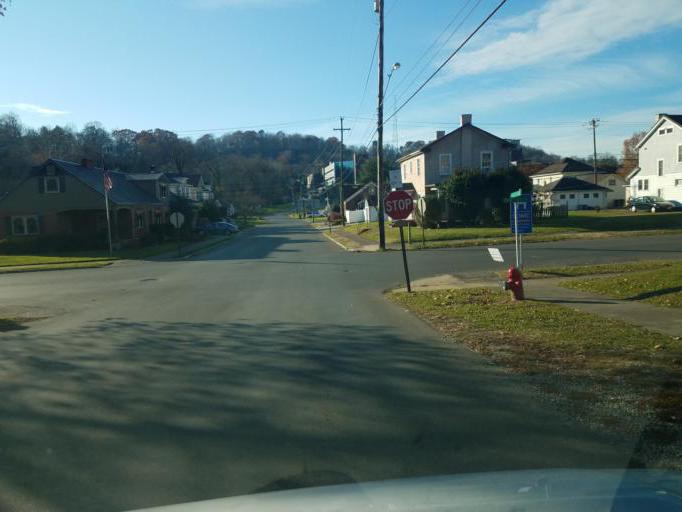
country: US
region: Ohio
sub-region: Scioto County
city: Portsmouth
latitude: 38.7522
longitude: -82.9745
